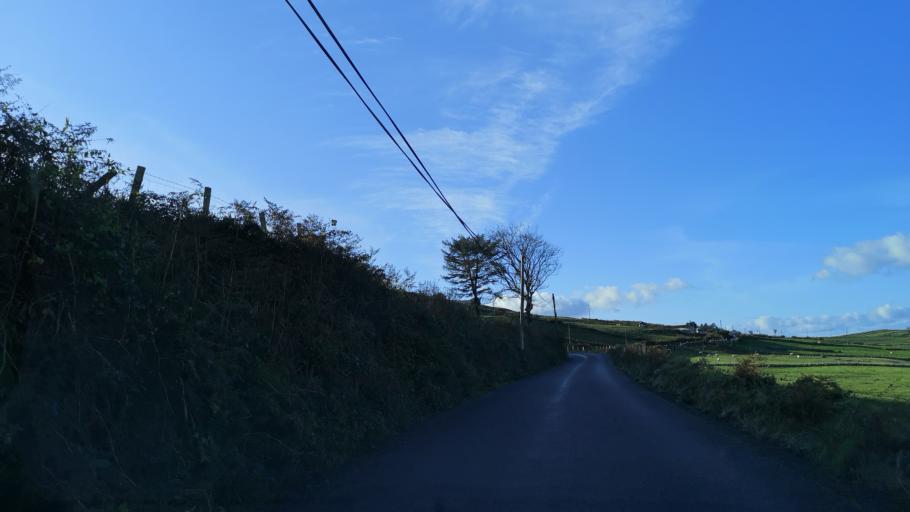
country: IE
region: Connaught
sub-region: County Galway
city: Clifden
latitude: 53.5062
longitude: -10.0852
